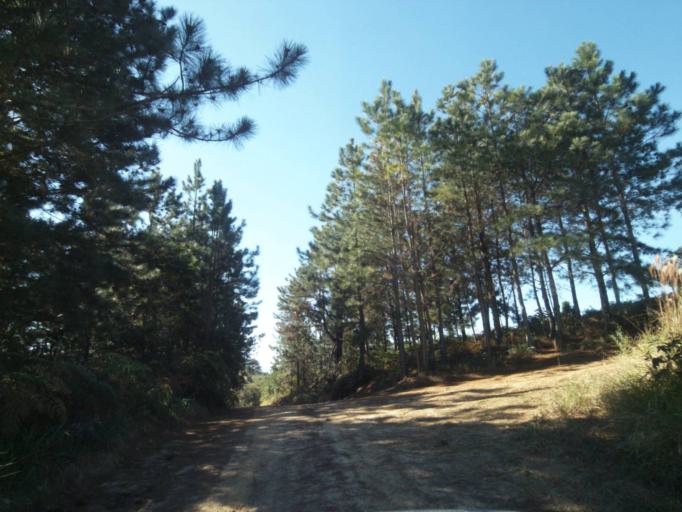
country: BR
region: Parana
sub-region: Tibagi
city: Tibagi
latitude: -24.5698
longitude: -50.4715
